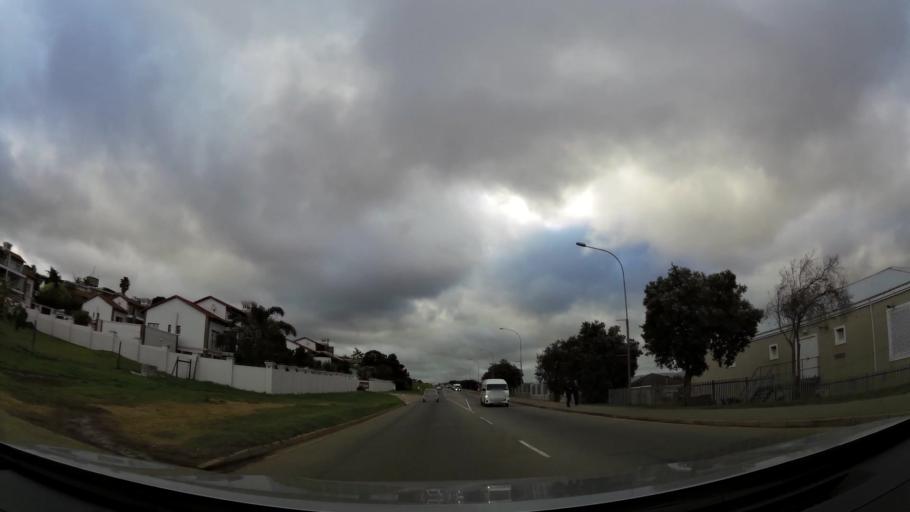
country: ZA
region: Western Cape
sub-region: Eden District Municipality
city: Plettenberg Bay
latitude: -34.0534
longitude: 23.3647
